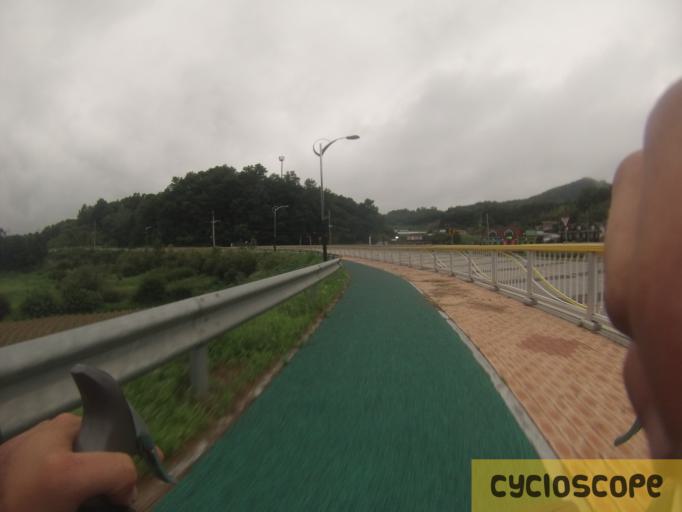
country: KR
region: Chungcheongnam-do
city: Yesan
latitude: 36.7411
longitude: 126.8595
